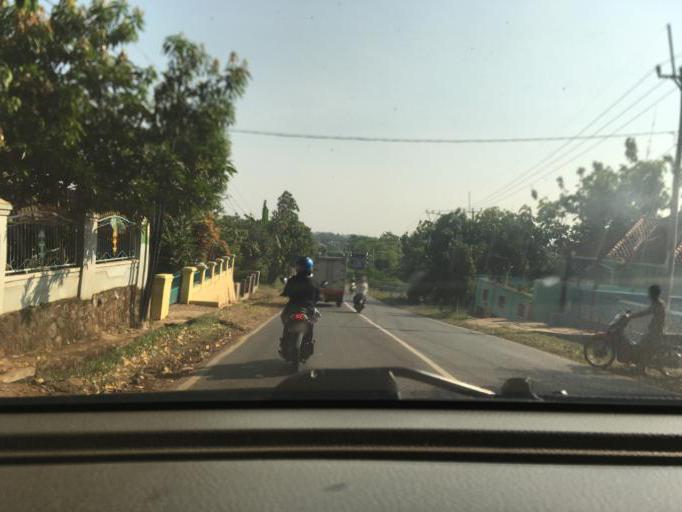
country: ID
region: West Java
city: Sumber
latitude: -6.8132
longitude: 108.5240
